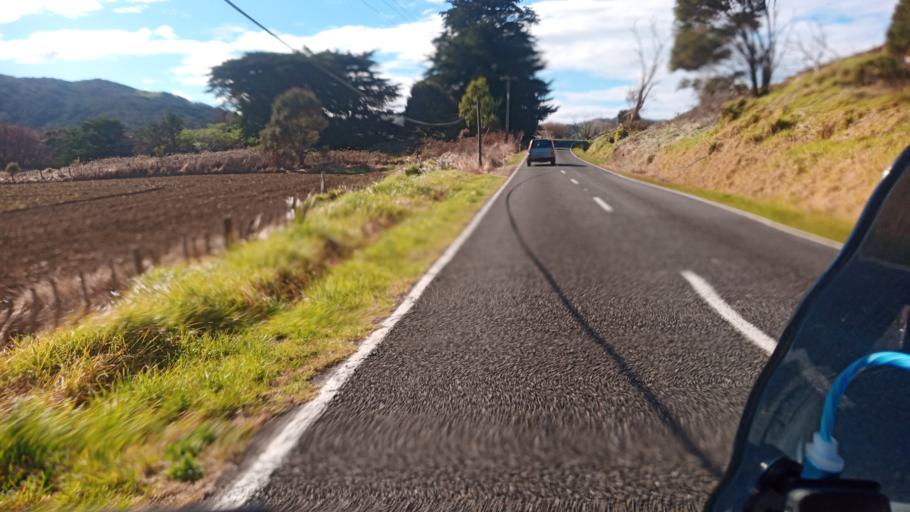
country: NZ
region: Gisborne
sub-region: Gisborne District
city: Gisborne
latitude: -38.2740
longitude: 178.2688
